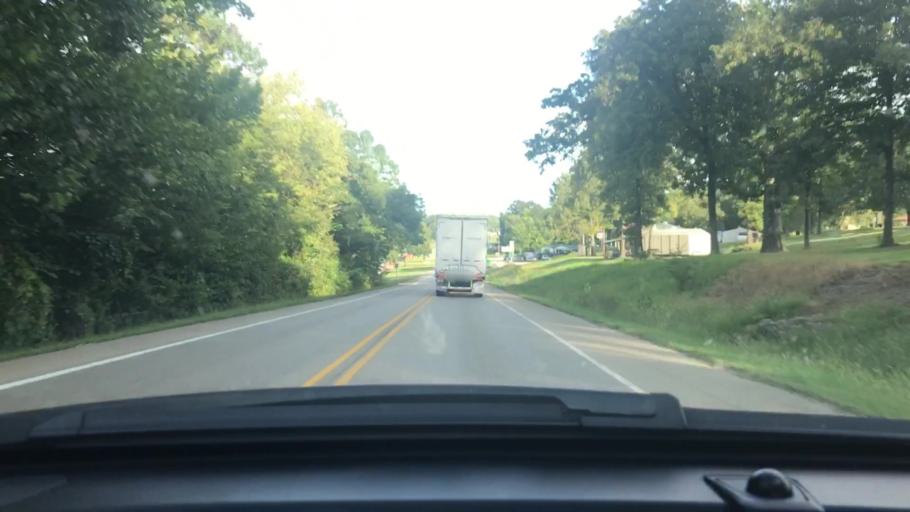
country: US
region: Arkansas
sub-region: Sharp County
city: Cherokee Village
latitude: 36.2381
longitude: -91.2573
